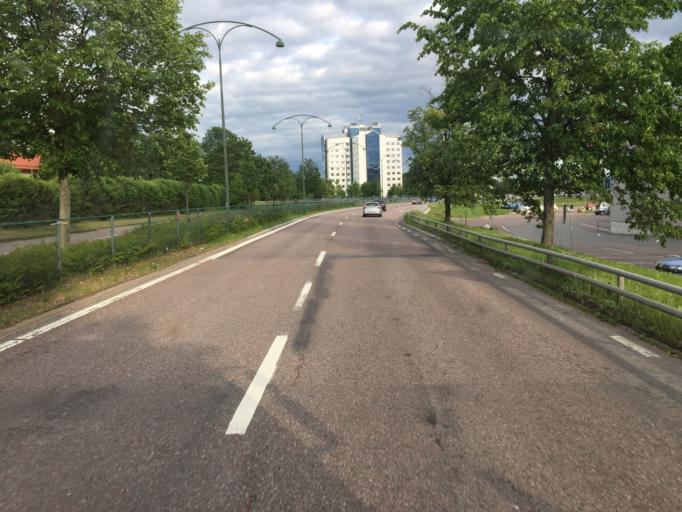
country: SE
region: Dalarna
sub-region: Borlange Kommun
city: Borlaenge
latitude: 60.4854
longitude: 15.4193
